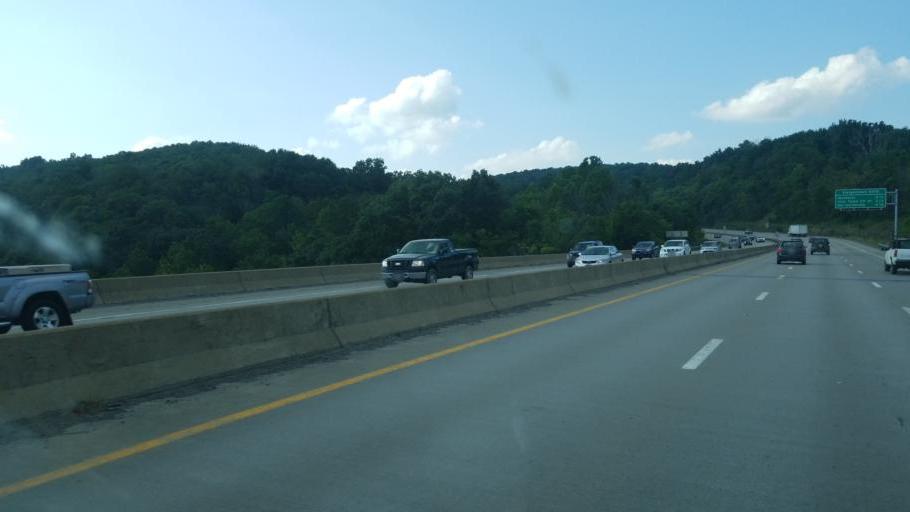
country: US
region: West Virginia
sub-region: Monongalia County
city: Westover
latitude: 39.5891
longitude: -79.9791
